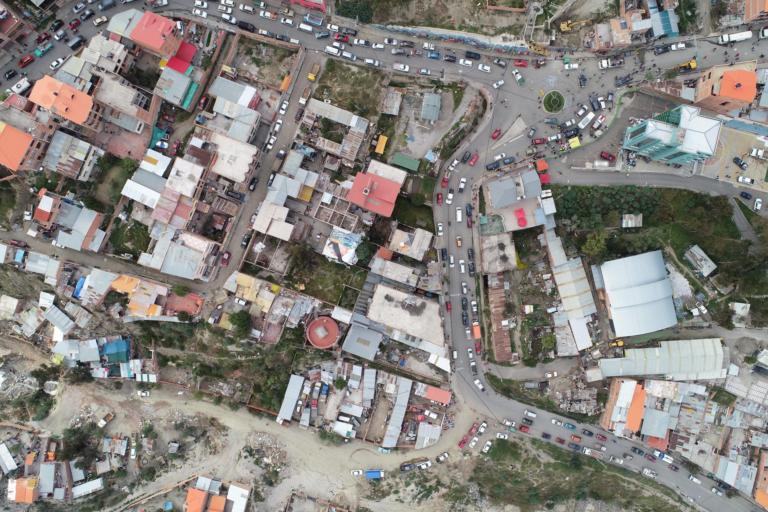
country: BO
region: La Paz
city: La Paz
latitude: -16.5206
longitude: -68.1259
